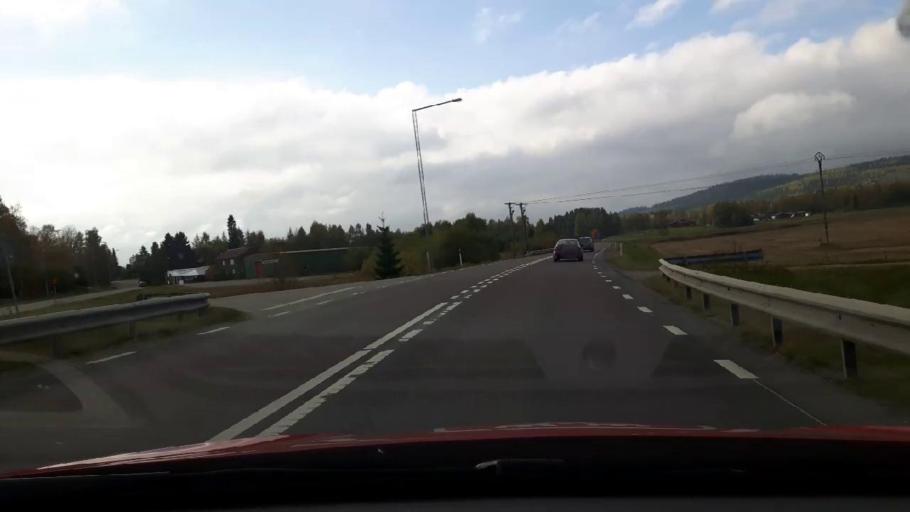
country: SE
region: Gaevleborg
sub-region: Bollnas Kommun
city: Arbra
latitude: 61.4879
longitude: 16.3723
